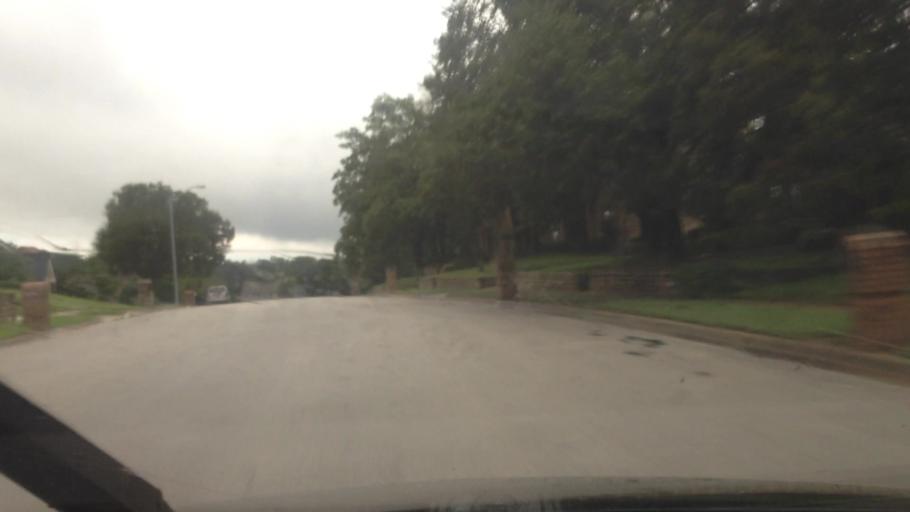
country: US
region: Texas
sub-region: Tarrant County
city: Colleyville
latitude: 32.8762
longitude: -97.1792
